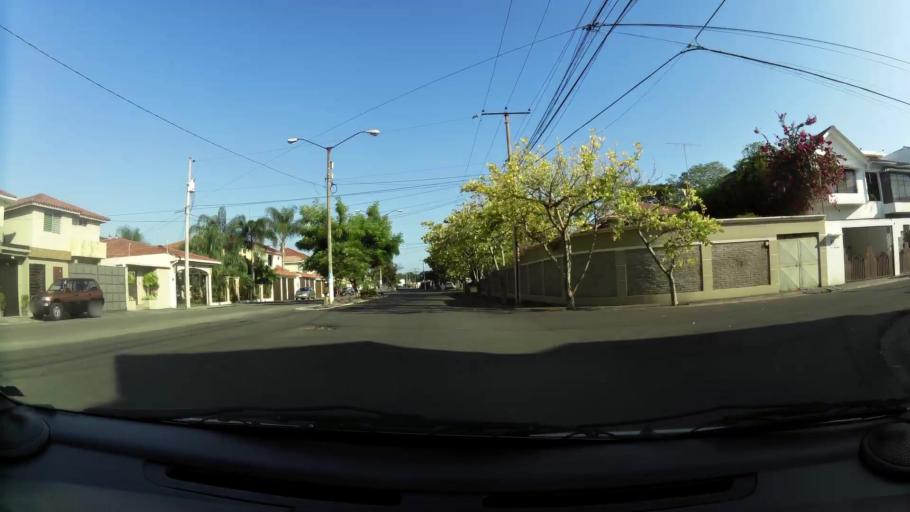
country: EC
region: Guayas
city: Santa Lucia
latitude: -2.1915
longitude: -79.9717
